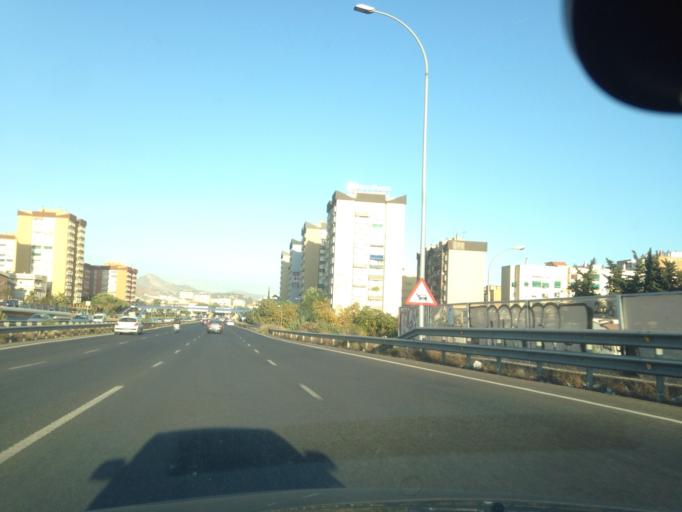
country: ES
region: Andalusia
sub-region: Provincia de Malaga
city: Malaga
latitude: 36.7137
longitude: -4.4541
